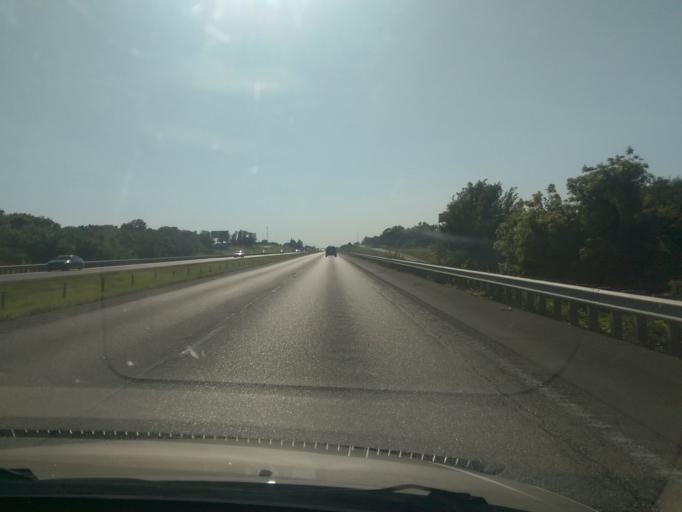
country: US
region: Missouri
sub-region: Lafayette County
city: Odessa
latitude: 39.0051
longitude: -93.8695
